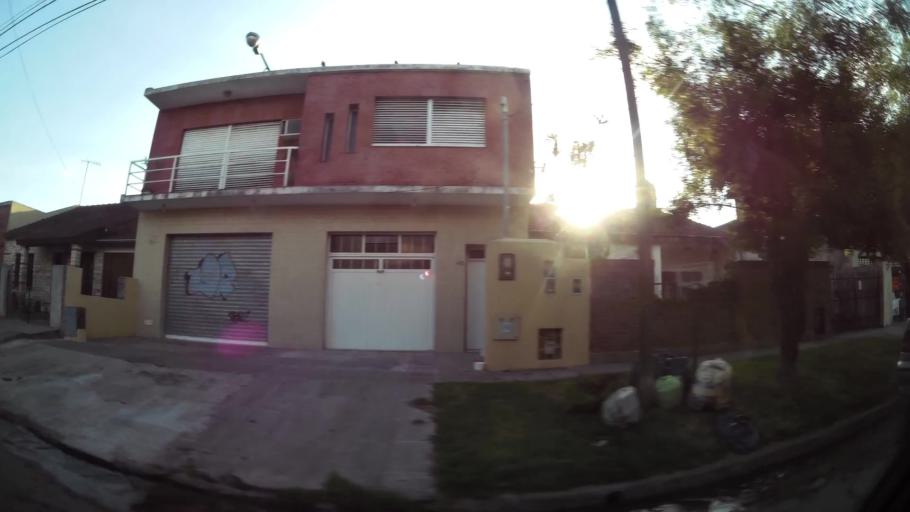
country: AR
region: Buenos Aires
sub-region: Partido de Tigre
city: Tigre
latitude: -34.4546
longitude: -58.6373
